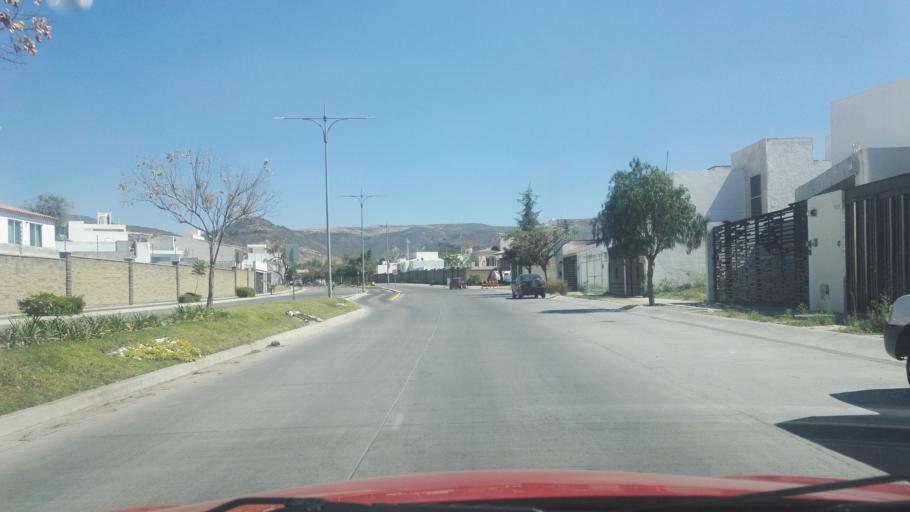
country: MX
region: Guanajuato
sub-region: Leon
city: Medina
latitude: 21.1276
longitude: -101.6086
